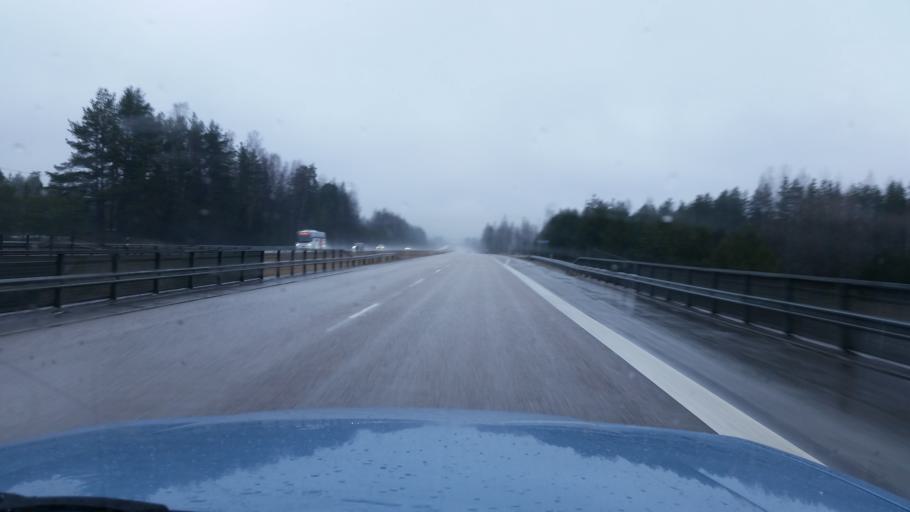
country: FI
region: Uusimaa
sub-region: Helsinki
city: Nurmijaervi
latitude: 60.5017
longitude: 24.8511
